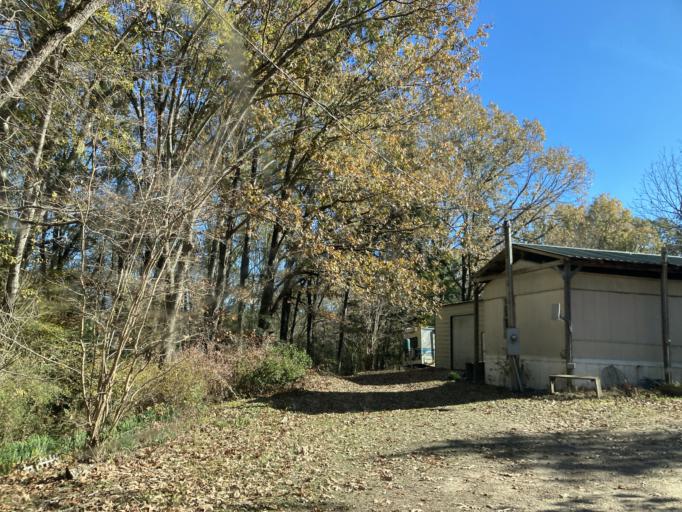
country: US
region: Mississippi
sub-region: Hinds County
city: Lynchburg
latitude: 32.5942
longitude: -90.4947
